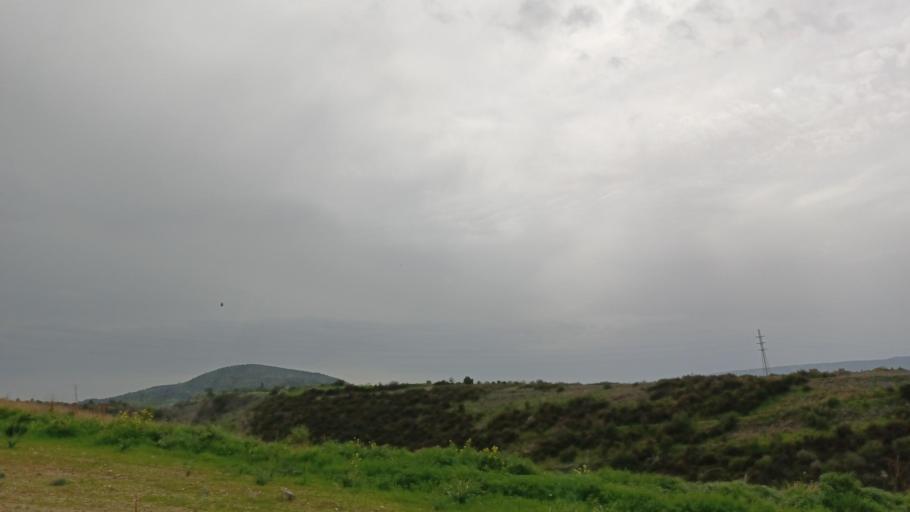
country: CY
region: Pafos
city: Polis
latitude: 35.0491
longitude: 32.4759
